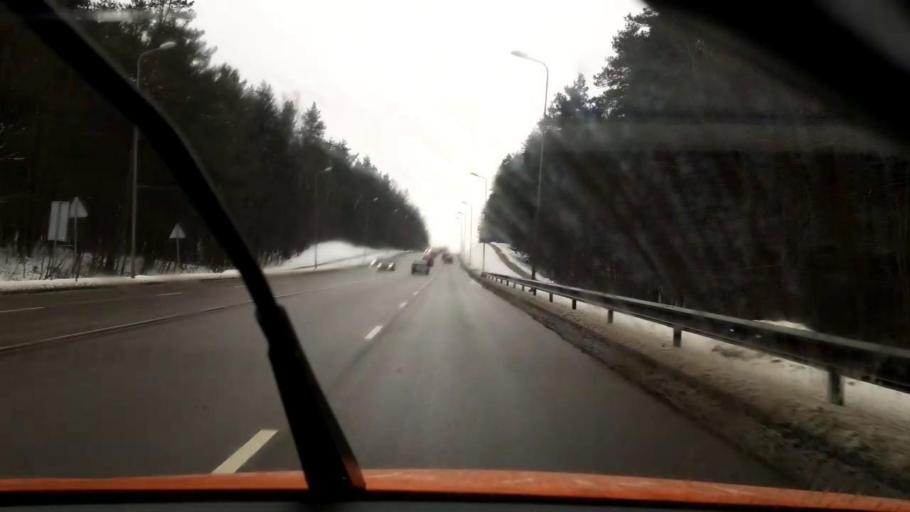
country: LT
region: Vilnius County
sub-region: Vilnius
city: Fabijoniskes
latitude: 54.7596
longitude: 25.2721
